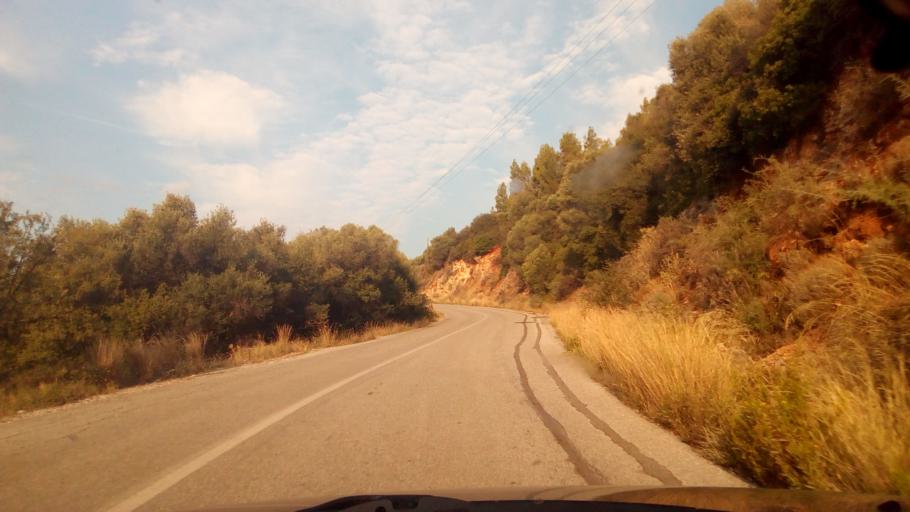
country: GR
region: West Greece
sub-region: Nomos Aitolias kai Akarnanias
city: Nafpaktos
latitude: 38.4085
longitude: 21.9360
